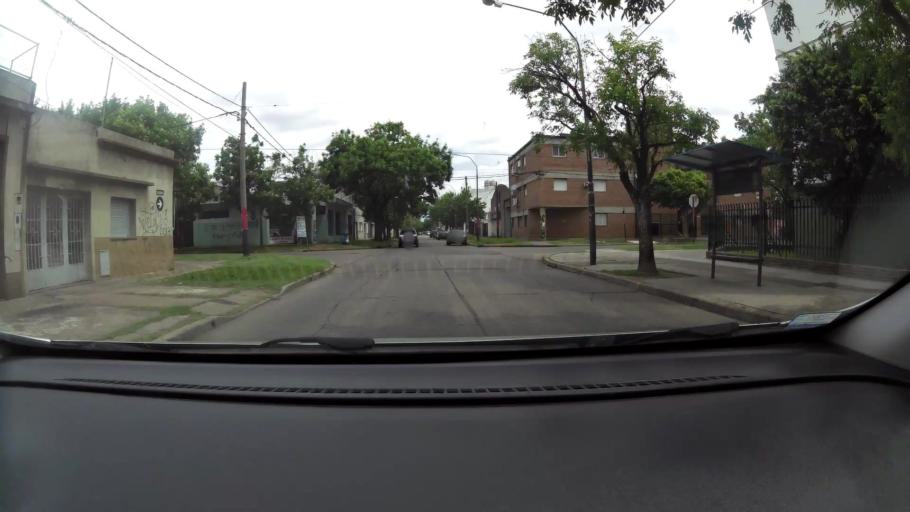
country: AR
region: Santa Fe
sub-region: Departamento de Rosario
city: Rosario
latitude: -32.9706
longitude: -60.6530
